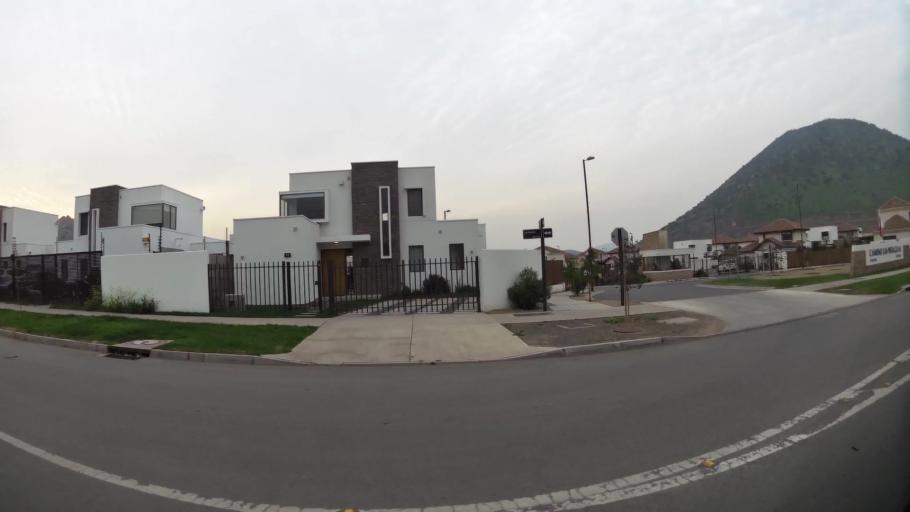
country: CL
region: Santiago Metropolitan
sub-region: Provincia de Chacabuco
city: Chicureo Abajo
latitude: -33.3166
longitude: -70.6525
